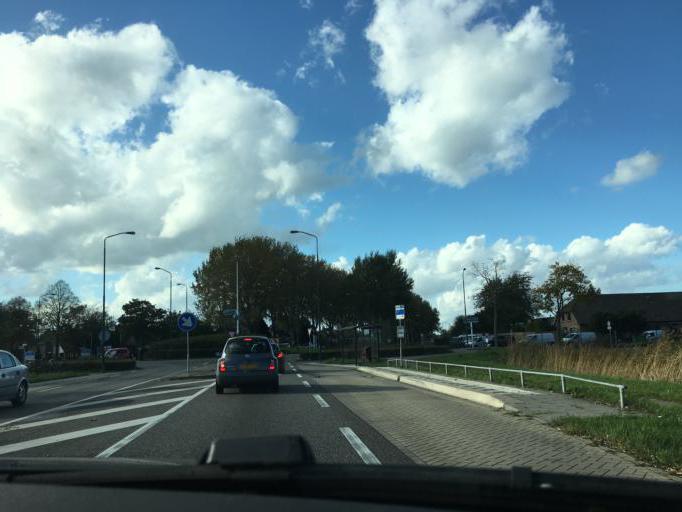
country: NL
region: North Brabant
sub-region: Gemeente Veghel
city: Eerde
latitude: 51.6037
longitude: 5.5037
